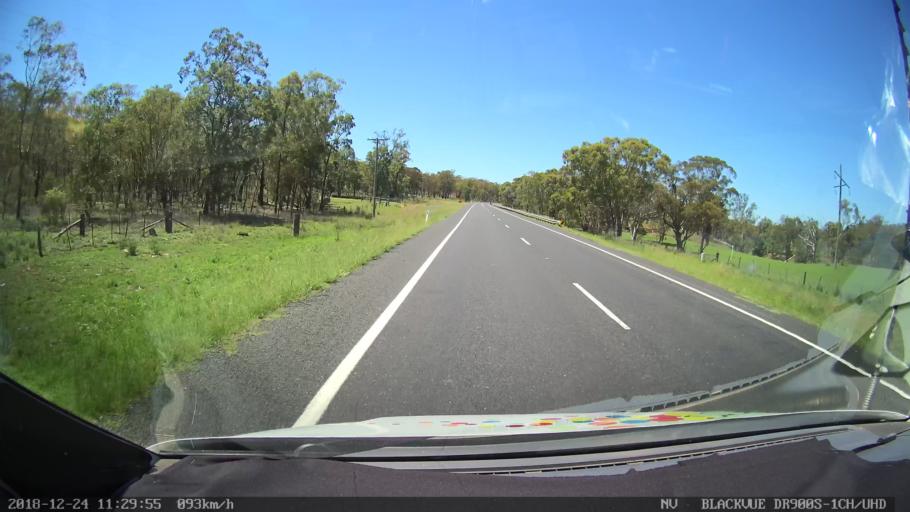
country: AU
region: New South Wales
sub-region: Upper Hunter Shire
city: Merriwa
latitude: -32.1984
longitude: 150.4660
